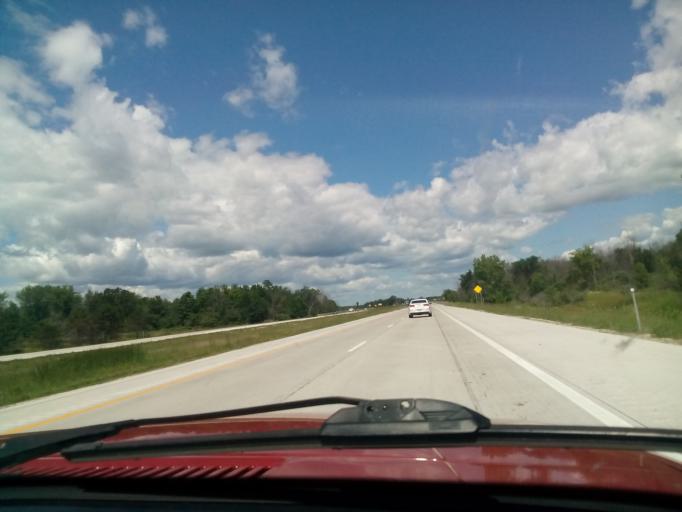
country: US
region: Michigan
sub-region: Bay County
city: Pinconning
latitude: 43.9055
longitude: -84.0200
